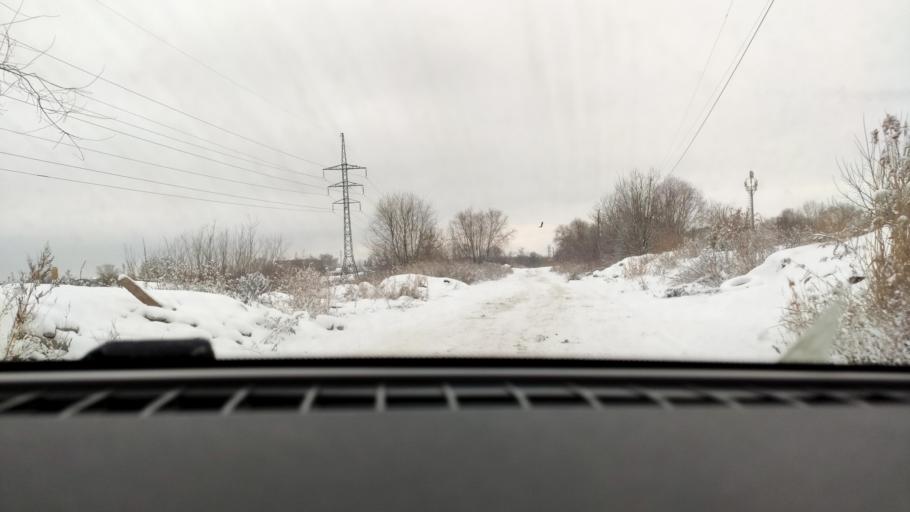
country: RU
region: Samara
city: Samara
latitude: 53.1324
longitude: 50.1146
